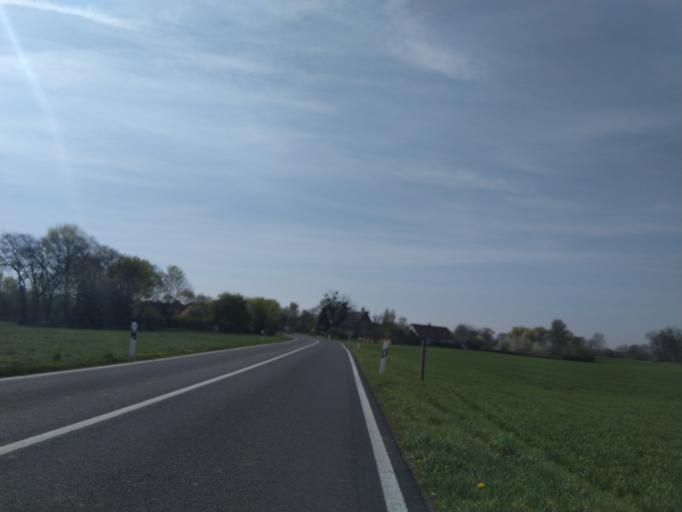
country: DE
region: Brandenburg
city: Wriezen
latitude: 52.7320
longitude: 14.1672
